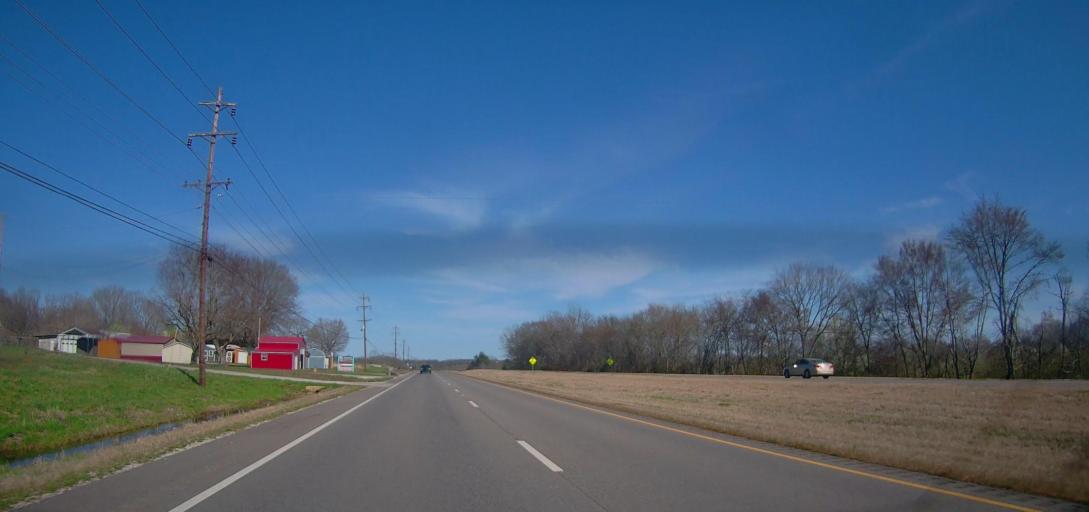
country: US
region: Alabama
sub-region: Lauderdale County
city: Killen
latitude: 34.8600
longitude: -87.4283
